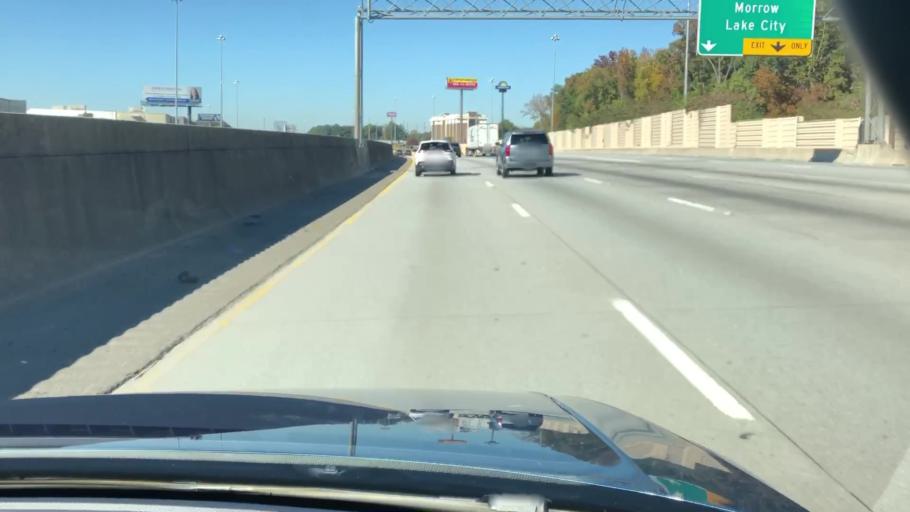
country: US
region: Georgia
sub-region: Clayton County
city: Morrow
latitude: 33.5743
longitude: -84.3355
